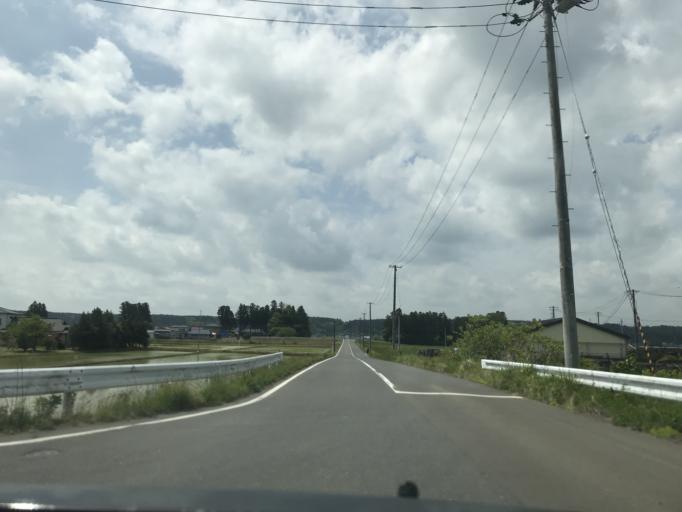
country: JP
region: Miyagi
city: Furukawa
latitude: 38.7523
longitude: 140.9367
